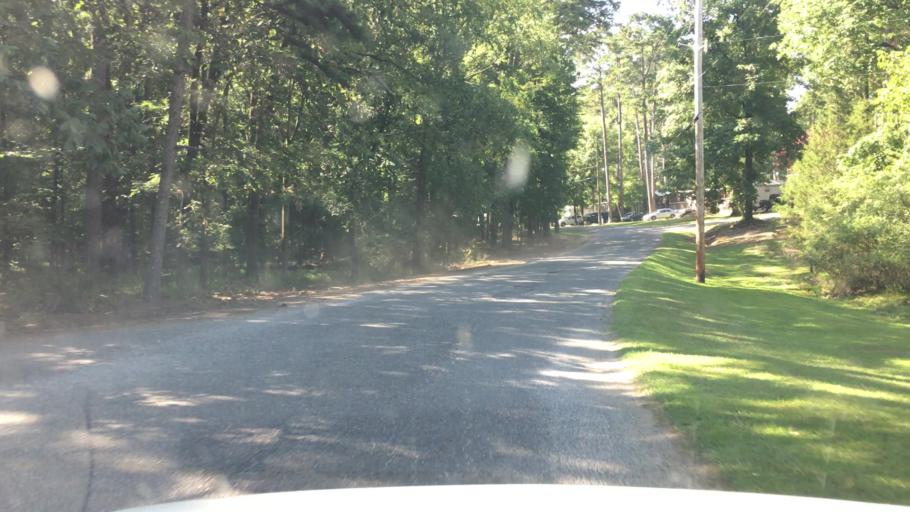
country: US
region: Arkansas
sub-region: Garland County
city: Piney
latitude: 34.5455
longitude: -93.3610
